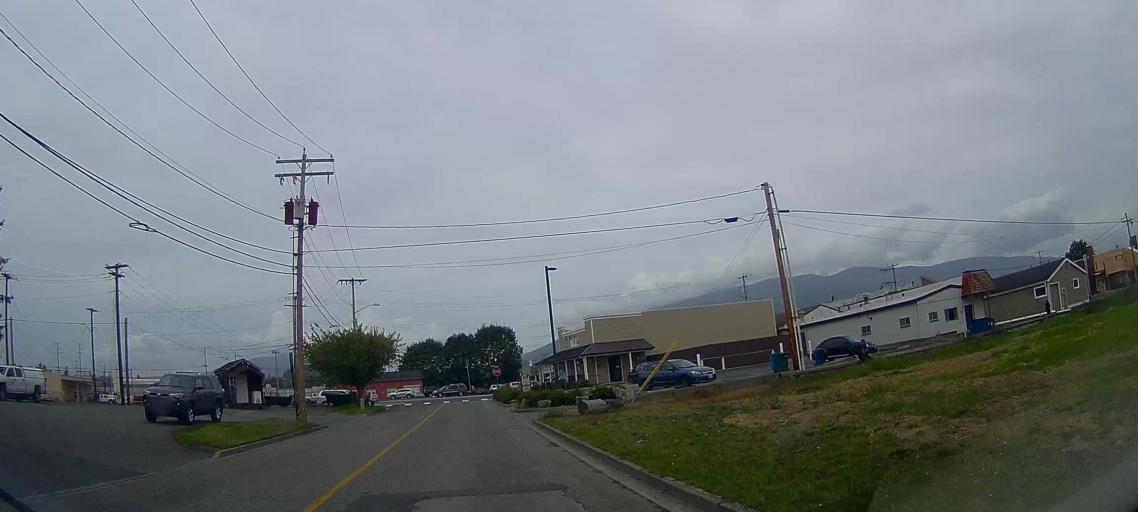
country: US
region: Washington
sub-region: Skagit County
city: Sedro-Woolley
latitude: 48.5027
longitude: -122.2401
